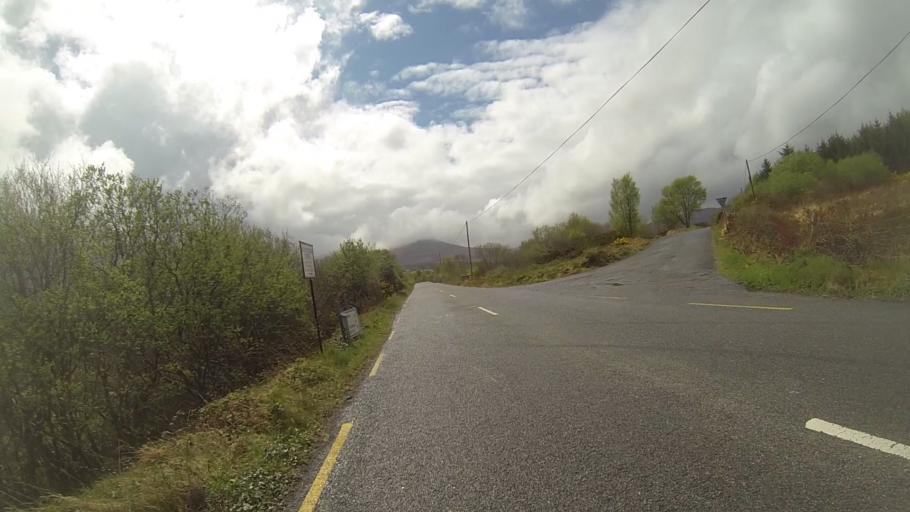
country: IE
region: Munster
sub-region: Ciarrai
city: Kenmare
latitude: 51.8945
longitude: -9.7593
